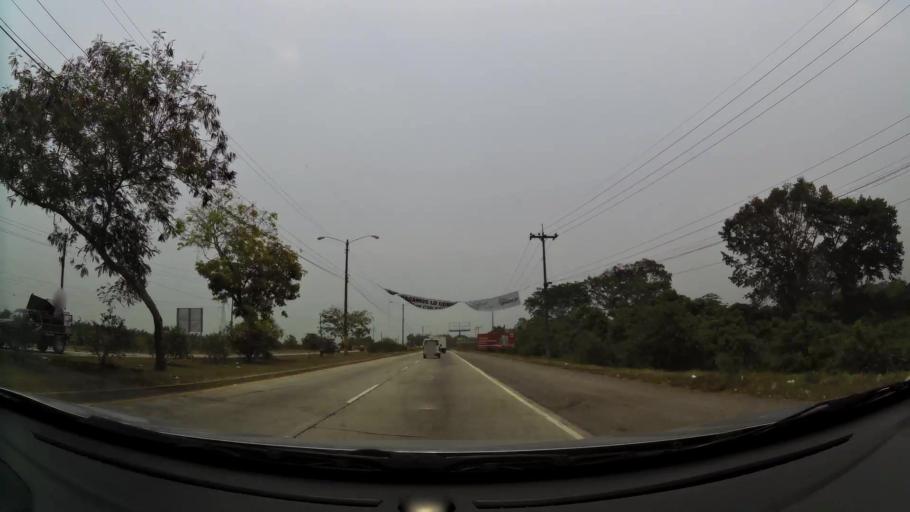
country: HN
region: Yoro
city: El Progreso
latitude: 15.4119
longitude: -87.8489
